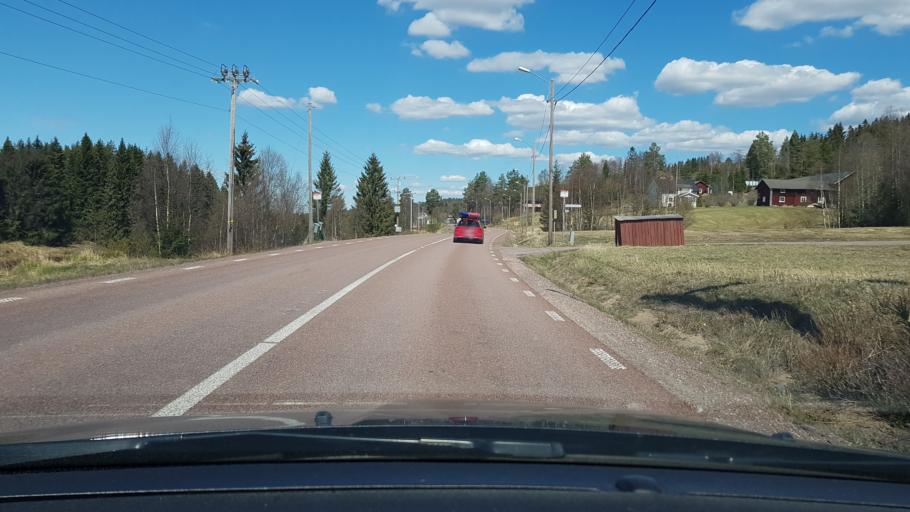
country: SE
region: Dalarna
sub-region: Malung-Saelens kommun
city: Malung
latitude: 61.0841
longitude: 13.3233
